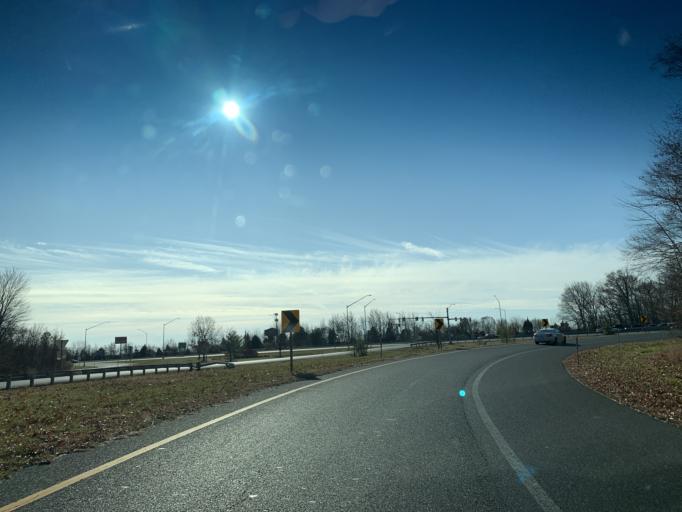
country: US
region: Maryland
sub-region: Harford County
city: Edgewood
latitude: 39.4560
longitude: -76.3075
